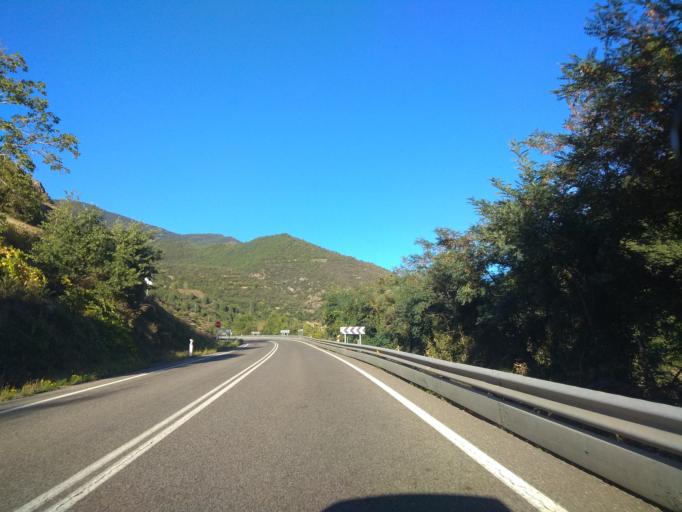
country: ES
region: Catalonia
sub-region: Provincia de Lleida
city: el Pont de Bar
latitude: 42.3688
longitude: 1.5966
